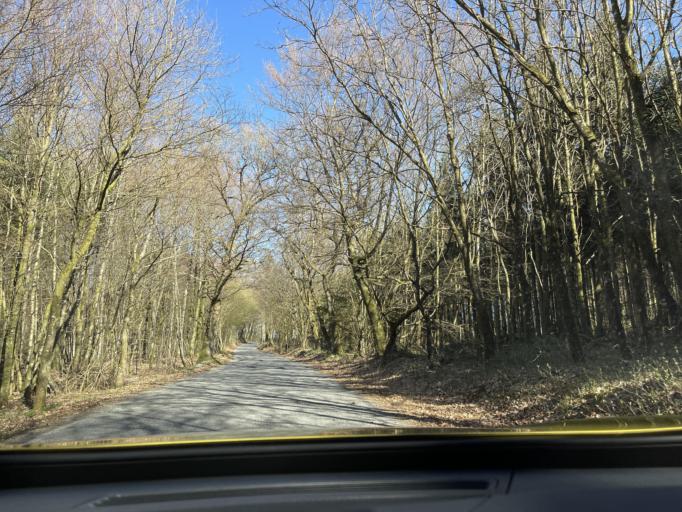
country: DK
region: Central Jutland
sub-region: Silkeborg Kommune
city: Kjellerup
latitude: 56.2469
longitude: 9.4745
